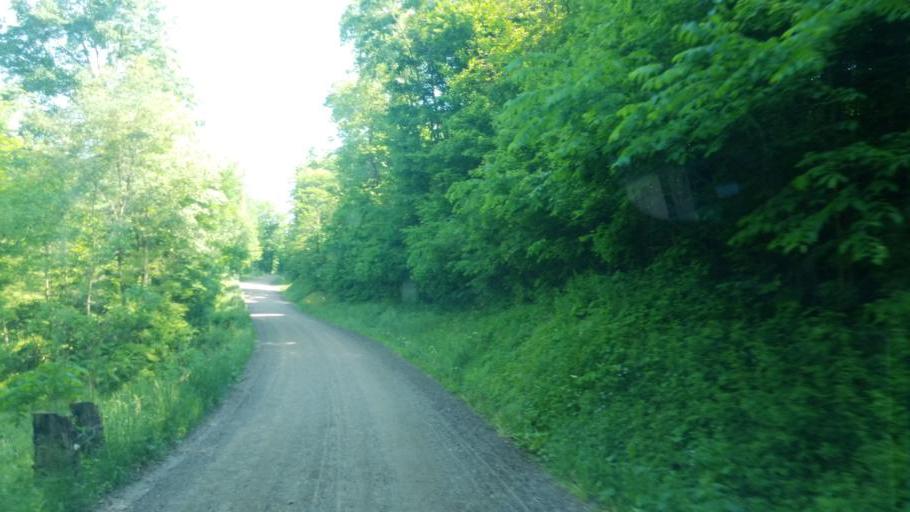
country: US
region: Ohio
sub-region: Holmes County
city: Millersburg
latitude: 40.4491
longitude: -81.8046
